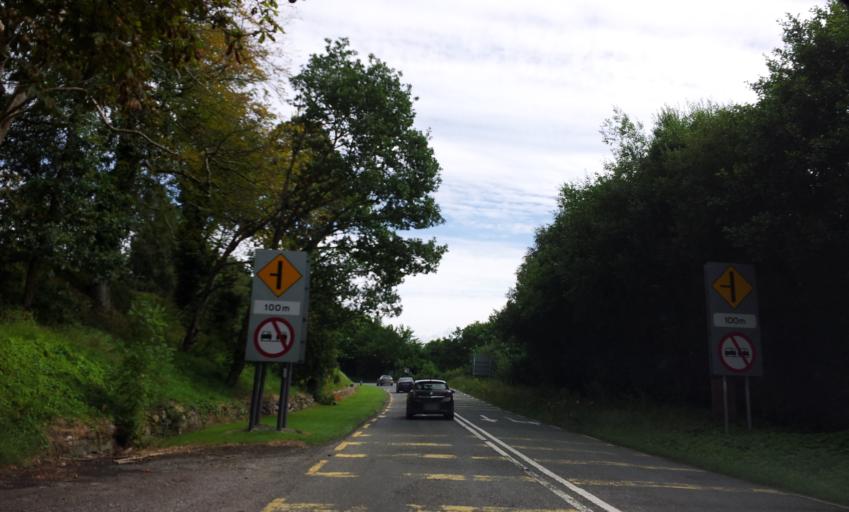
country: IE
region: Munster
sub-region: Ciarrai
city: Cill Airne
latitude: 52.0753
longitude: -9.6306
